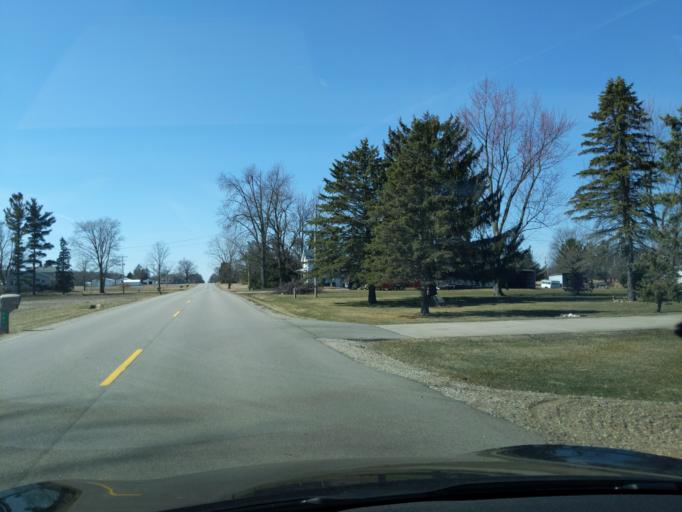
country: US
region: Michigan
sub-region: Eaton County
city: Grand Ledge
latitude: 42.7266
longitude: -84.8281
